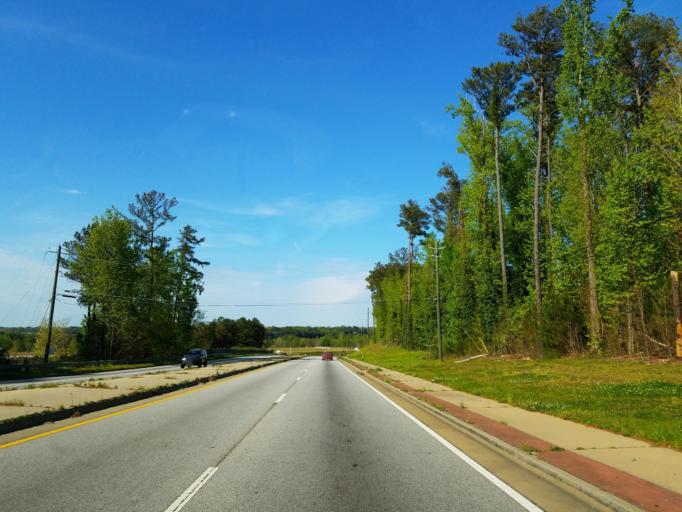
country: US
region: Georgia
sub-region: Cobb County
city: Mableton
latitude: 33.7772
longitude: -84.5121
